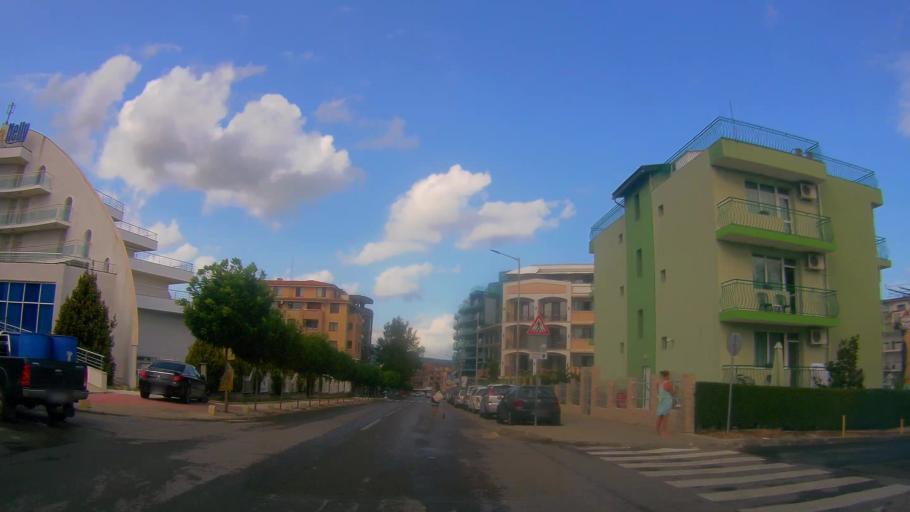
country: BG
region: Burgas
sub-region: Obshtina Primorsko
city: Primorsko
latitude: 42.2717
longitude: 27.7509
